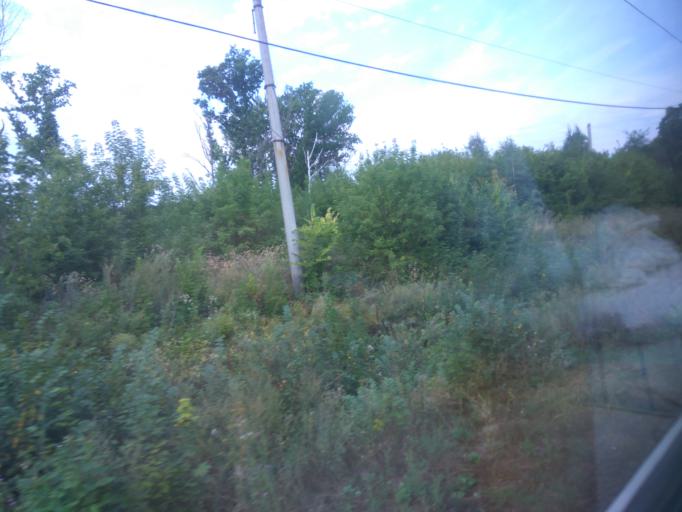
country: RU
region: Saratov
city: Rtishchevo
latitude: 52.2228
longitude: 43.8618
